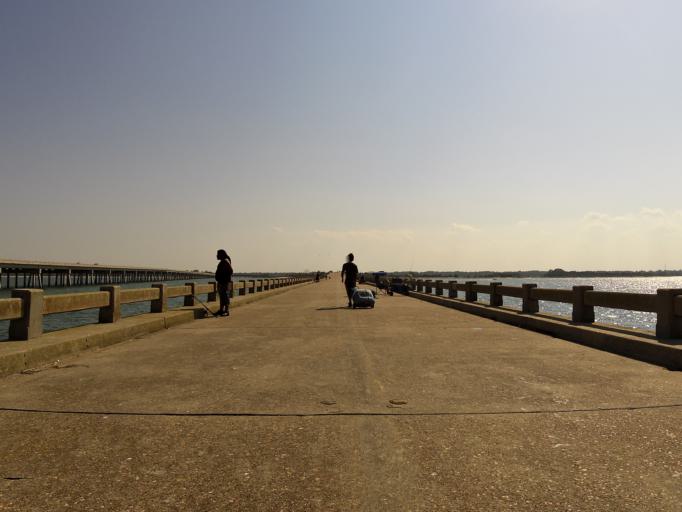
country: US
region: Florida
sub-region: Nassau County
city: Fernandina Beach
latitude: 30.5207
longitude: -81.4483
